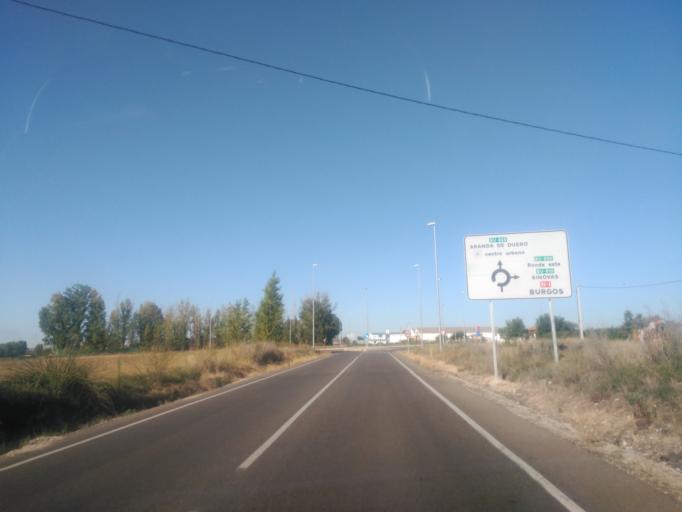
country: ES
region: Castille and Leon
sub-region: Provincia de Burgos
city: Fresnillo de las Duenas
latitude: 41.6760
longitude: -3.6576
